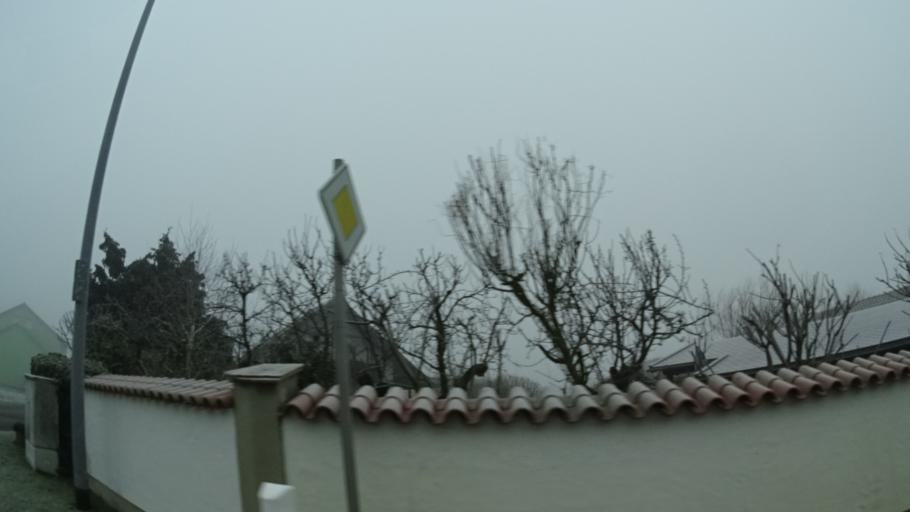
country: DE
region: Bavaria
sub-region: Regierungsbezirk Unterfranken
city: Michelau
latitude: 49.9320
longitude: 10.4301
